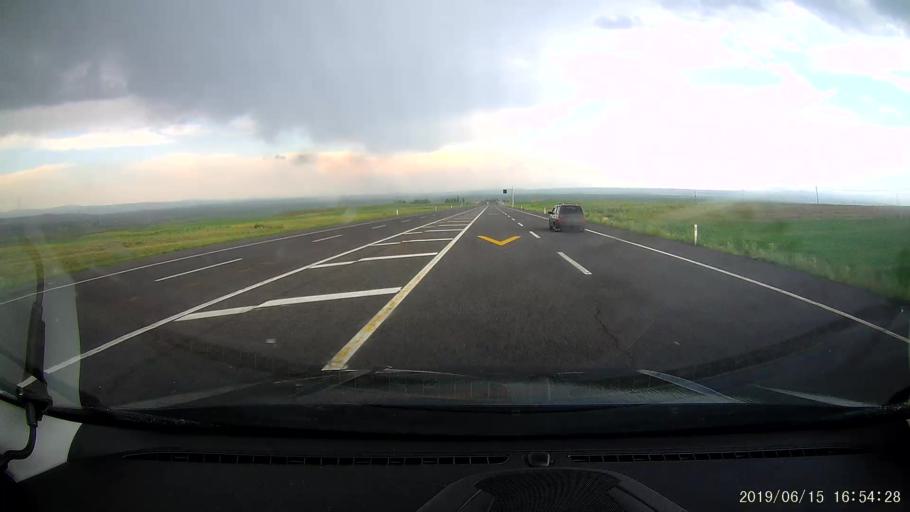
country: TR
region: Kars
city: Susuz
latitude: 40.7902
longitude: 43.1250
